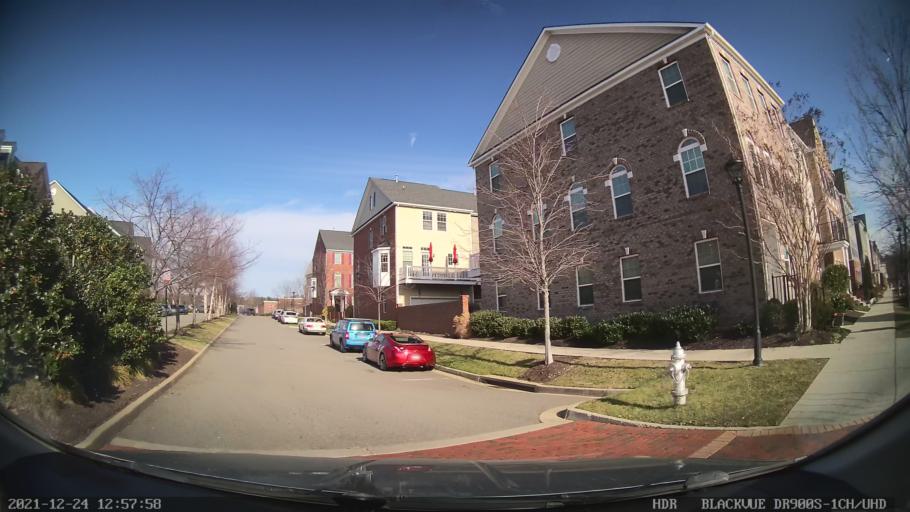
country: US
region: Virginia
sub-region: Henrico County
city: Short Pump
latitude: 37.6462
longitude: -77.5988
